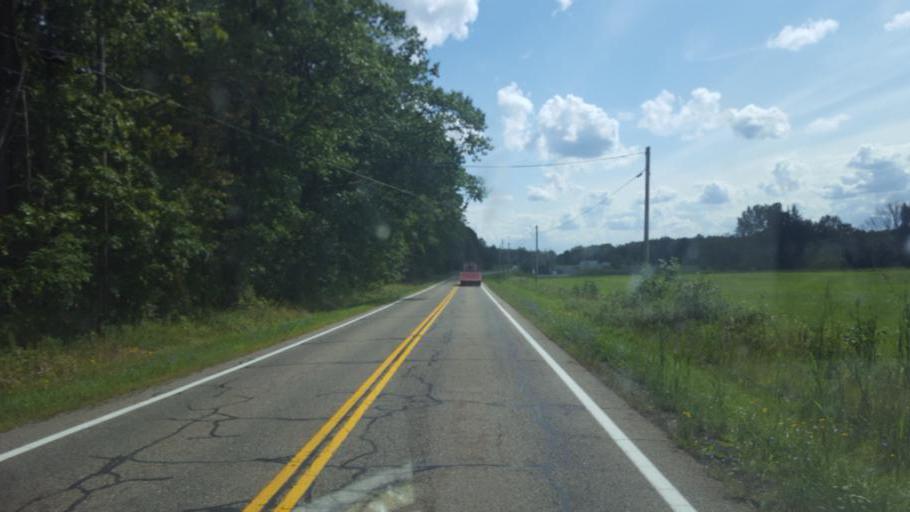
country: US
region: Ohio
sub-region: Portage County
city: Hiram
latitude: 41.2603
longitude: -81.1454
